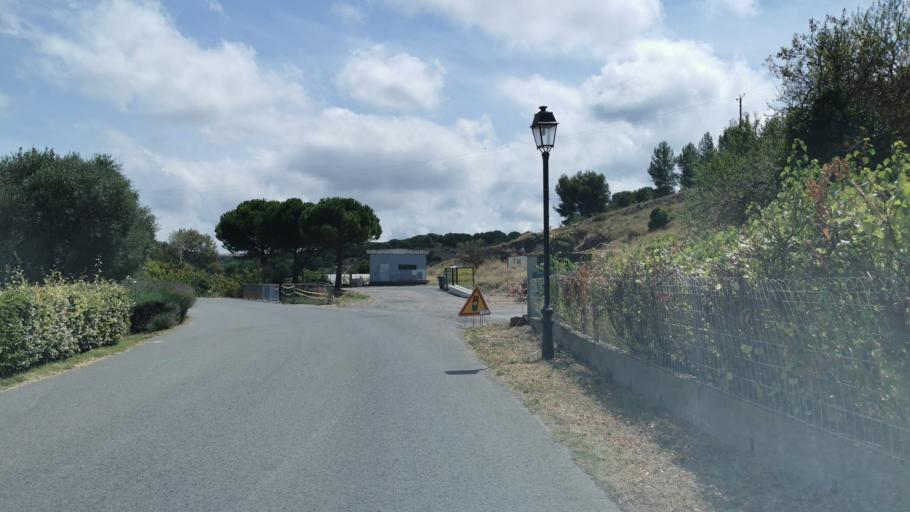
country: FR
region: Languedoc-Roussillon
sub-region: Departement de l'Aude
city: Bizanet
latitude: 43.1661
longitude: 2.8763
